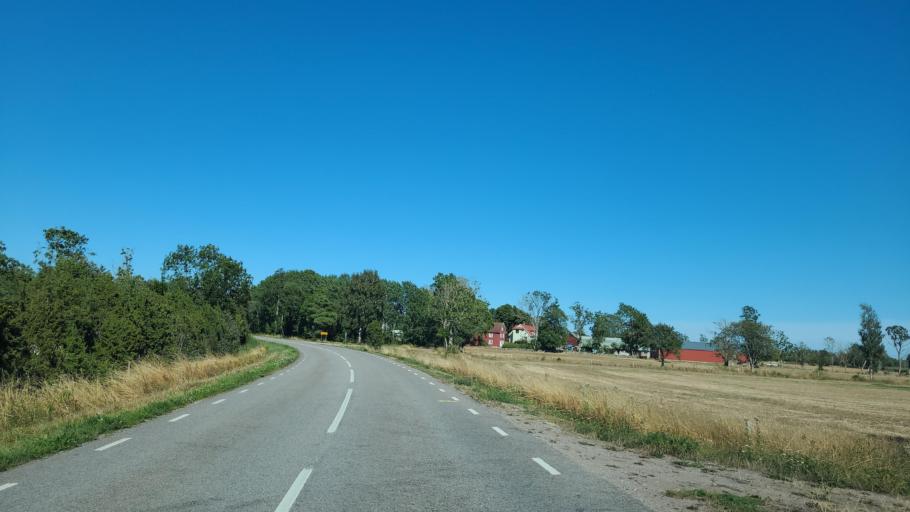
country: SE
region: Kalmar
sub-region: Borgholms Kommun
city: Borgholm
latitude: 56.9750
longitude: 16.8567
